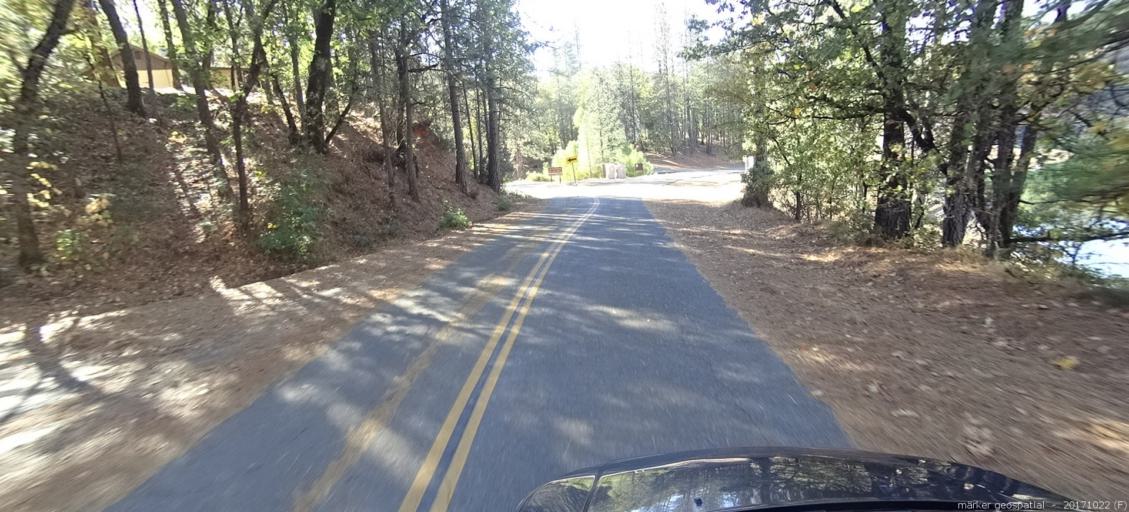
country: US
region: California
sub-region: Shasta County
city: Shasta Lake
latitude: 40.8430
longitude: -122.3518
